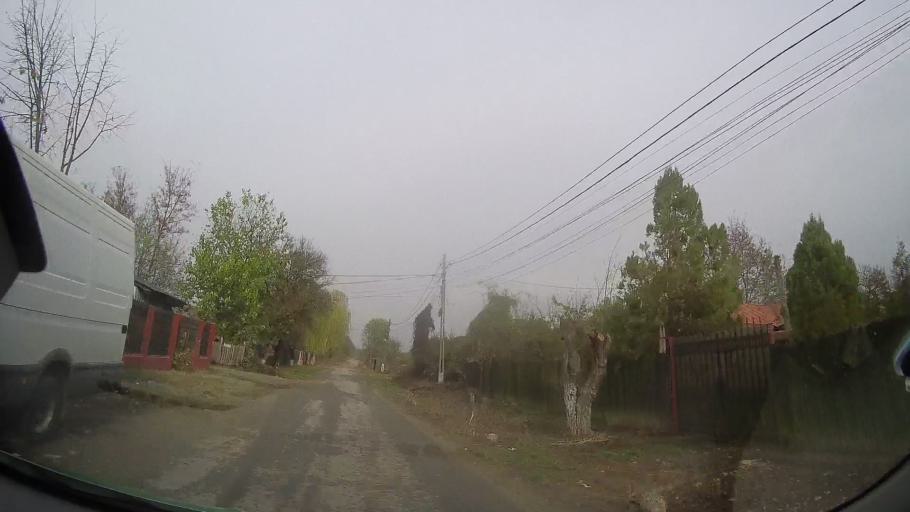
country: RO
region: Ilfov
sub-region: Comuna Ciolpani
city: Ciolpani
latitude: 44.7489
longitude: 26.1213
